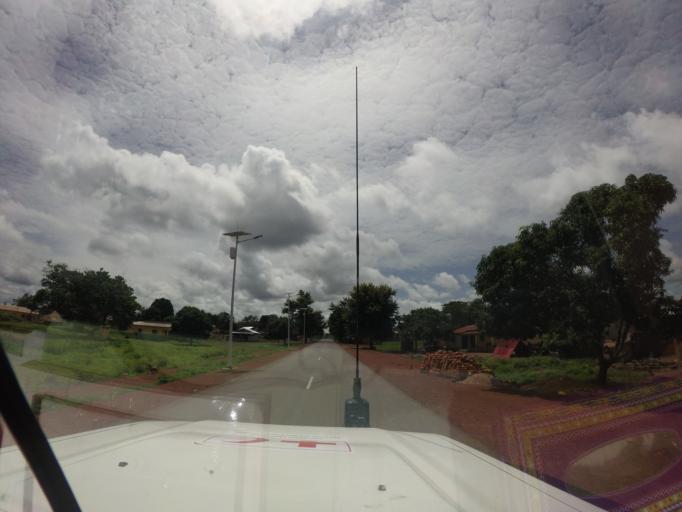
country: SL
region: Northern Province
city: Gberia Fotombu
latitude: 10.0690
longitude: -11.1205
